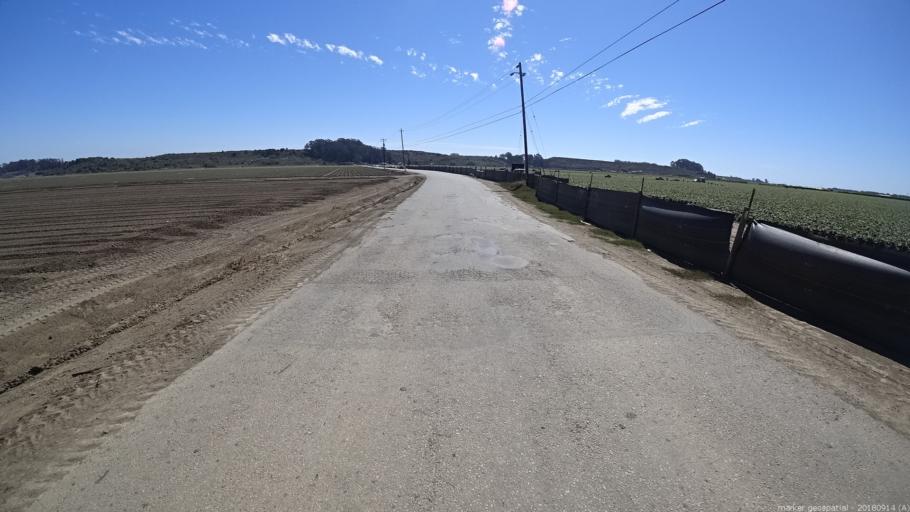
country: US
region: California
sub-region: Santa Cruz County
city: Watsonville
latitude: 36.8780
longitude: -121.7917
